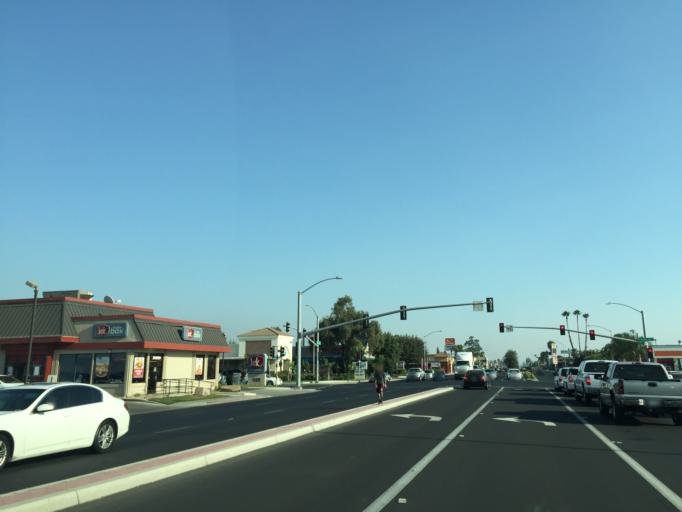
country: US
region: California
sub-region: Tulare County
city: Visalia
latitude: 36.3209
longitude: -119.3140
